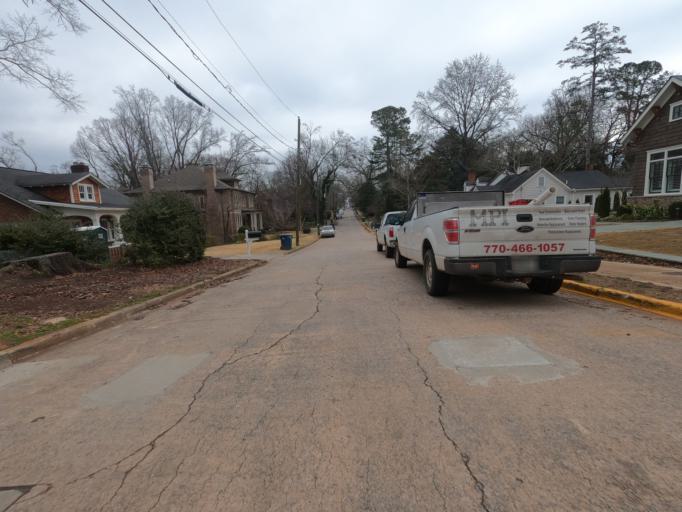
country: US
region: Georgia
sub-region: Clarke County
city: Athens
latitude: 33.9386
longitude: -83.3836
